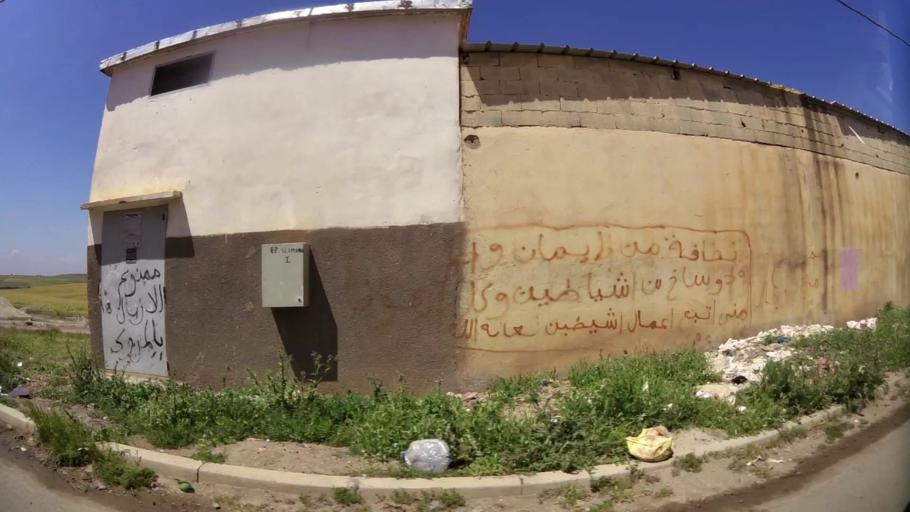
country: MA
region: Oriental
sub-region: Oujda-Angad
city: Oujda
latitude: 34.6824
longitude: -1.9606
